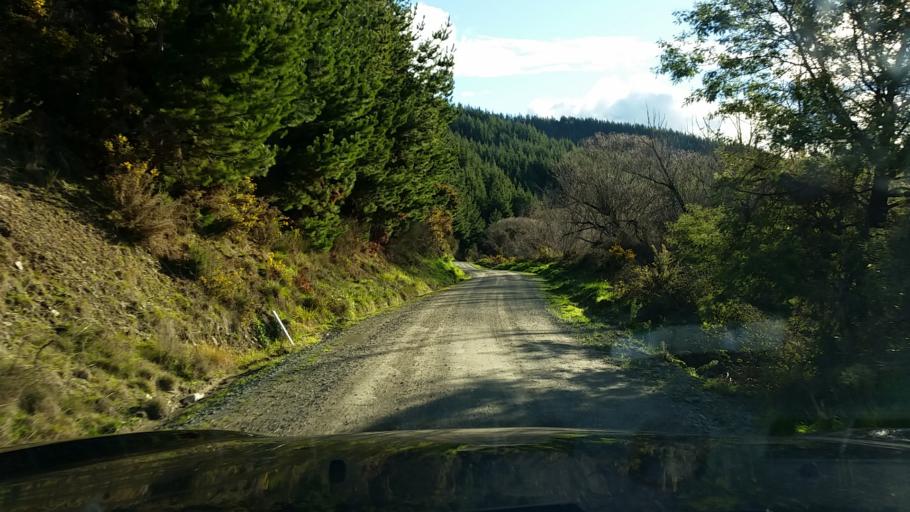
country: NZ
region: Nelson
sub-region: Nelson City
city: Nelson
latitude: -41.5632
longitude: 173.4367
